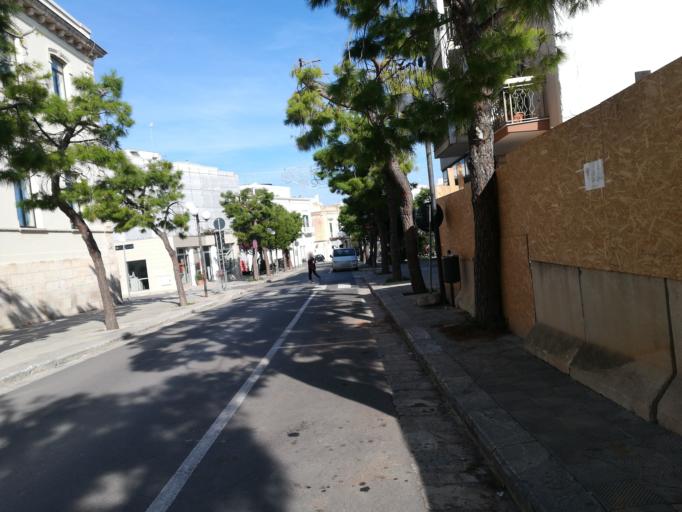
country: IT
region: Apulia
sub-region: Provincia di Bari
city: Polignano a Mare
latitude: 40.9925
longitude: 17.2194
